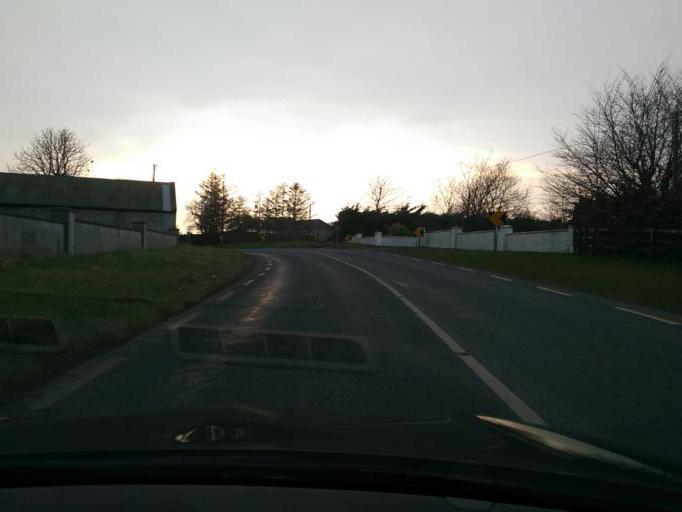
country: IE
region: Leinster
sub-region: An Longfort
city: Ballymahon
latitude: 53.5211
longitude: -7.8160
